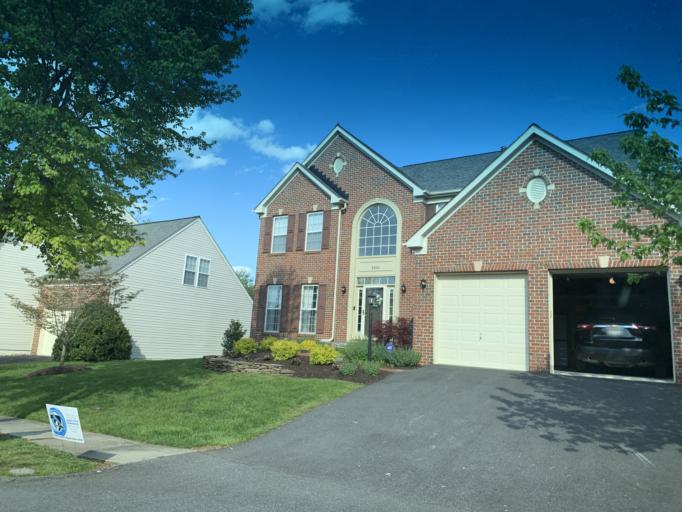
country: US
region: Maryland
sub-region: Baltimore County
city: White Marsh
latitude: 39.4048
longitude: -76.4344
